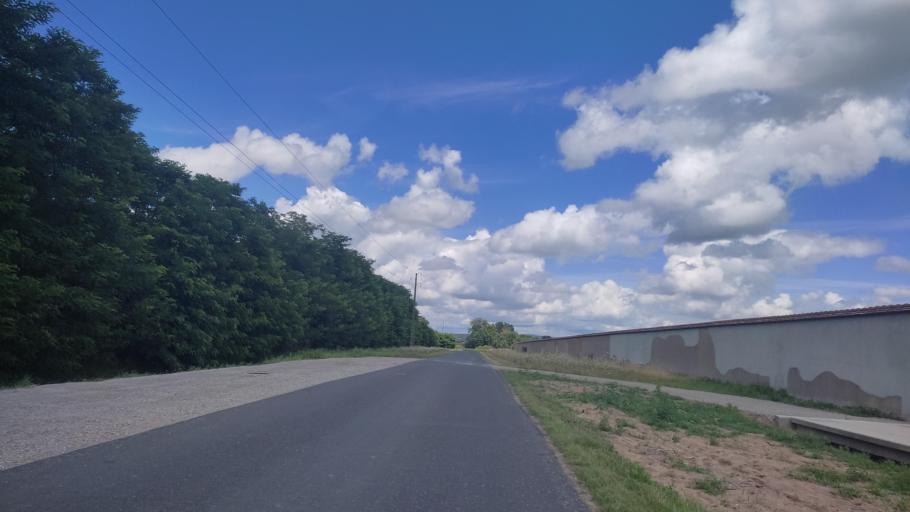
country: FR
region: Auvergne
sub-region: Departement de l'Allier
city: Dompierre-sur-Besbre
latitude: 46.5490
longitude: 3.7068
